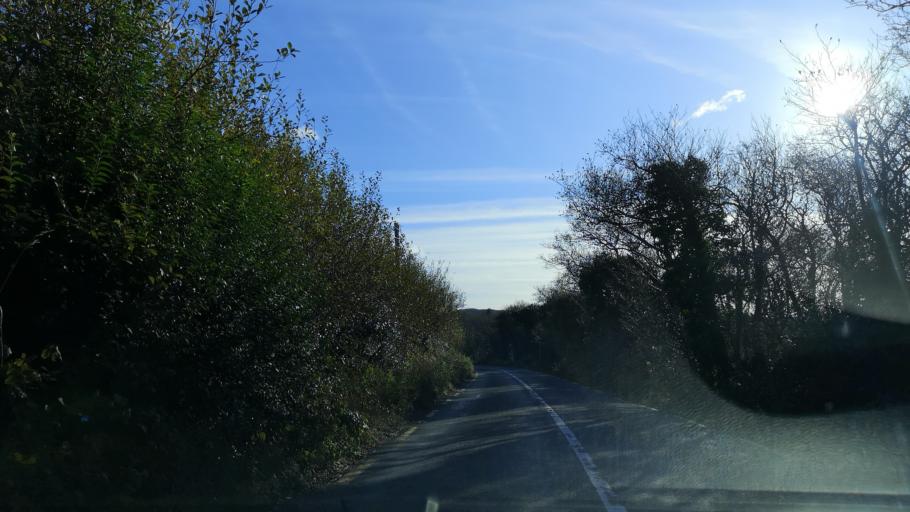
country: IE
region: Connaught
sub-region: County Galway
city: Clifden
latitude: 53.5463
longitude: -9.9740
